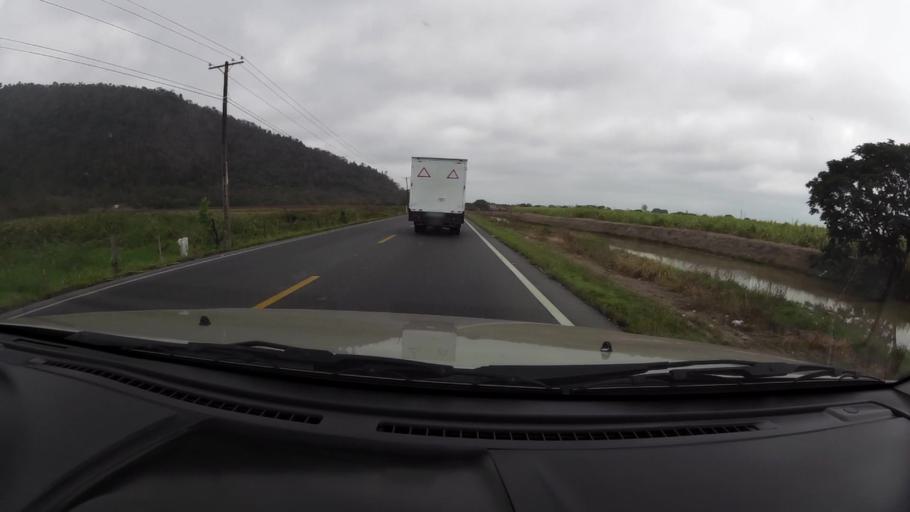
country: EC
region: Guayas
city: Naranjal
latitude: -2.4431
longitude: -79.6271
